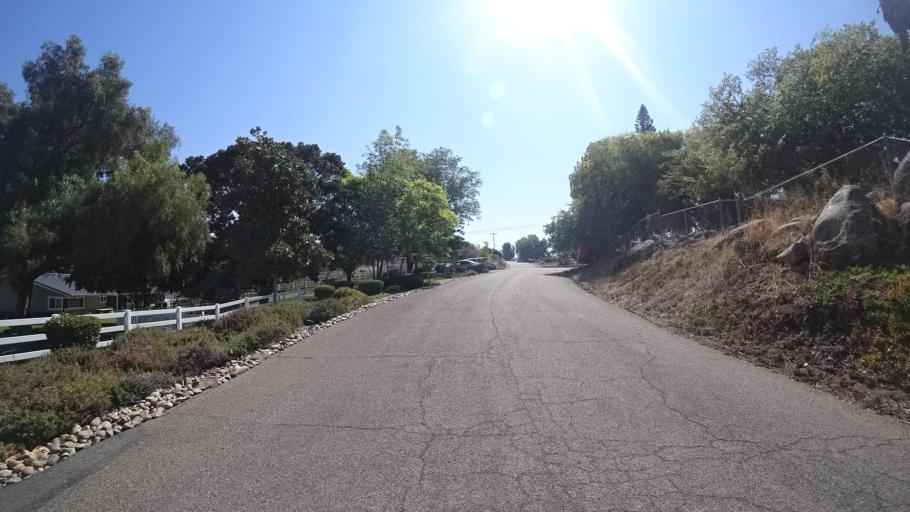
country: US
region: California
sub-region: San Diego County
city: Granite Hills
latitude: 32.7905
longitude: -116.9090
